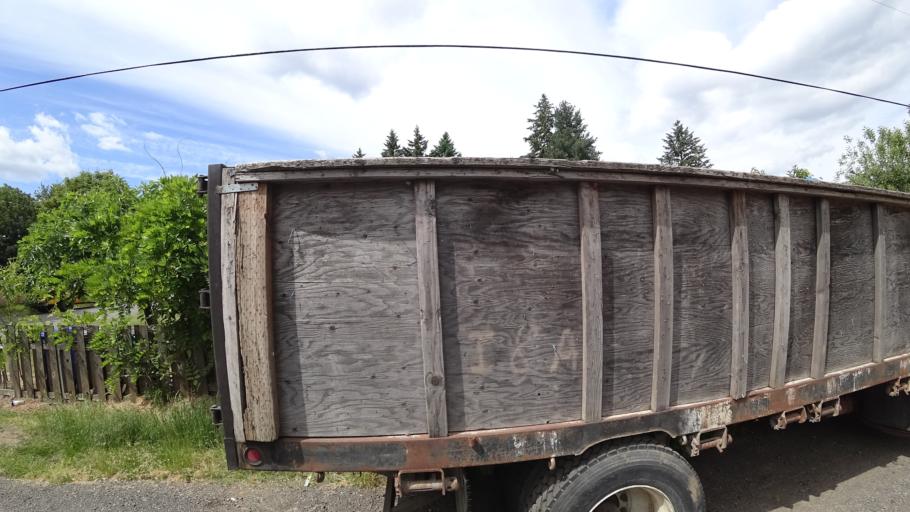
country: US
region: Oregon
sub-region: Multnomah County
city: Lents
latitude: 45.4848
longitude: -122.5523
